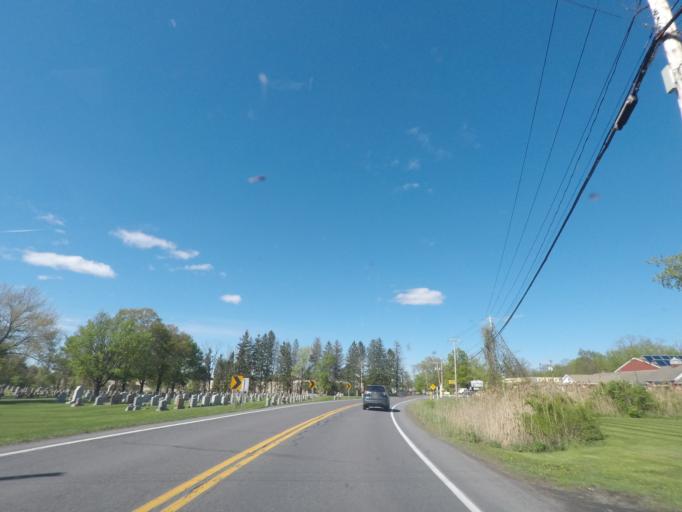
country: US
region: New York
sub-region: Albany County
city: Delmar
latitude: 42.5981
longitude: -73.7949
